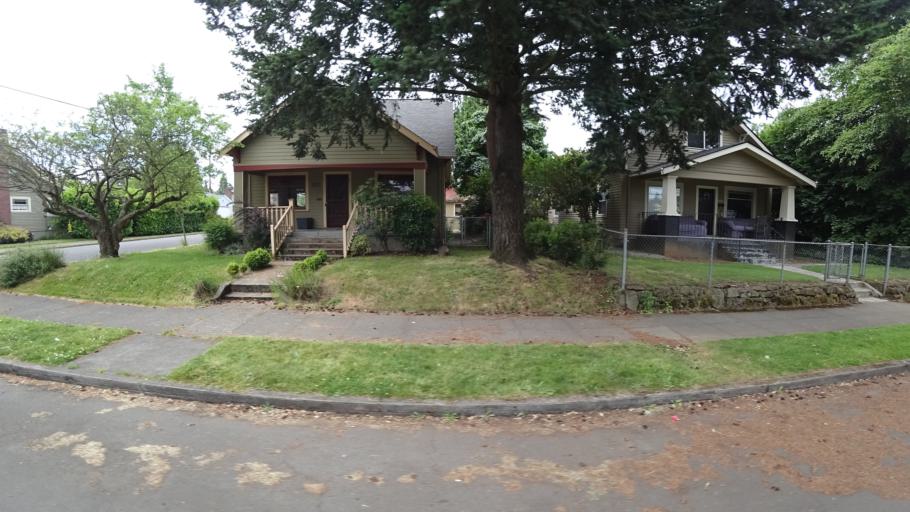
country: US
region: Oregon
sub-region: Multnomah County
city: Portland
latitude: 45.5785
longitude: -122.7256
